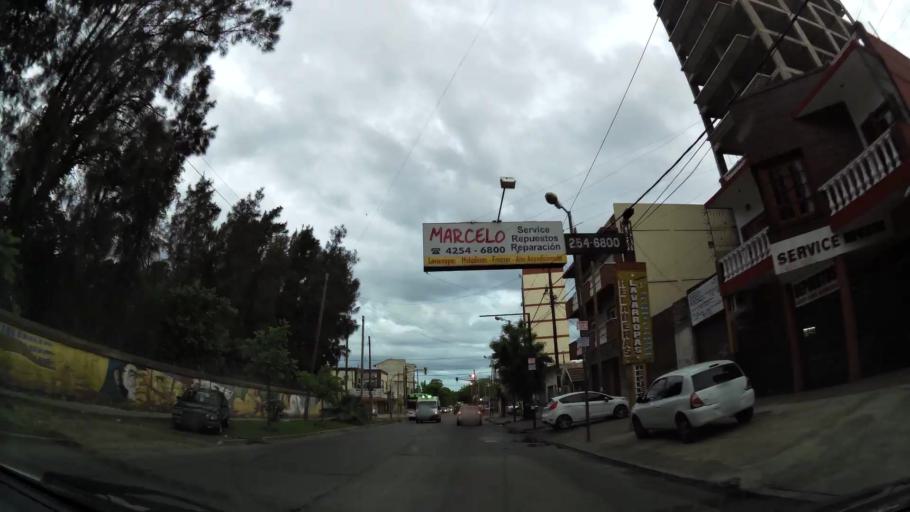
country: AR
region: Buenos Aires
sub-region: Partido de Quilmes
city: Quilmes
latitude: -34.7335
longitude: -58.2440
